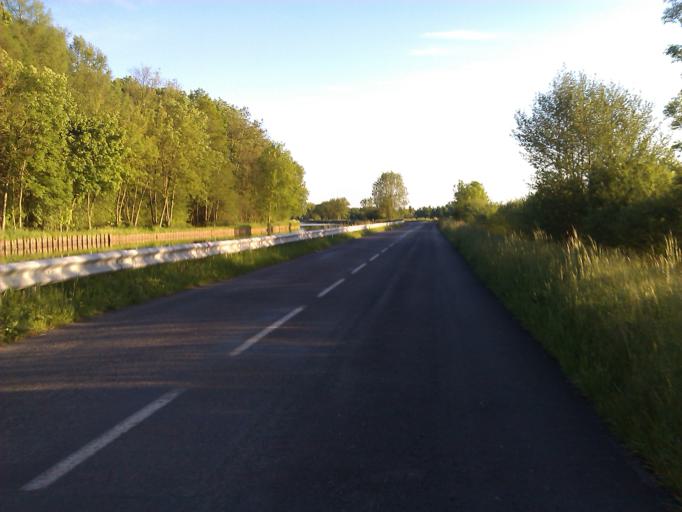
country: FR
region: Bourgogne
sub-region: Departement de Saone-et-Loire
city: Palinges
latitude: 46.5389
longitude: 4.2069
